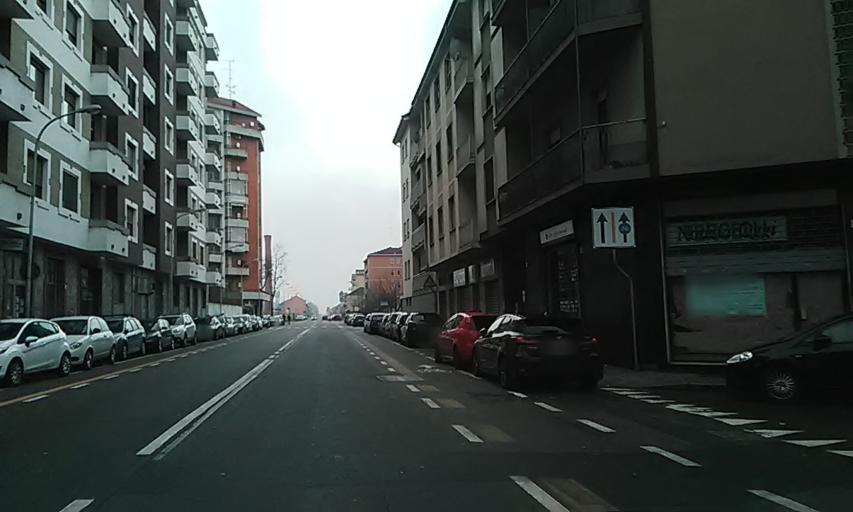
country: IT
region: Piedmont
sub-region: Provincia di Vercelli
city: Vercelli
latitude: 45.3195
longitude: 8.4135
